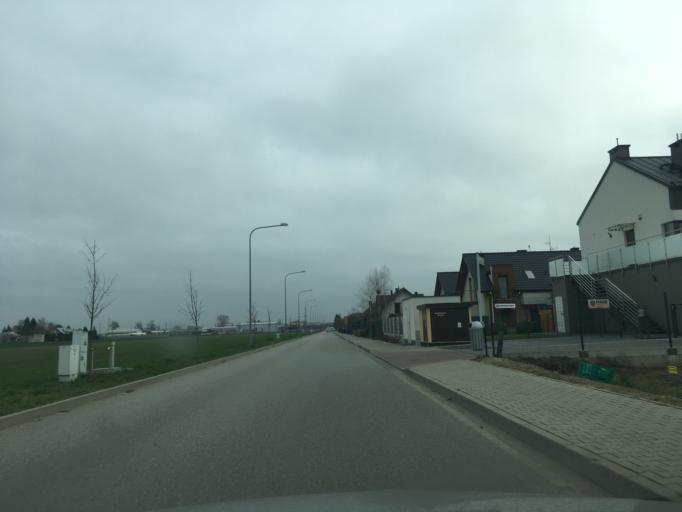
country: PL
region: Masovian Voivodeship
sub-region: Powiat piaseczynski
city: Lesznowola
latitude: 52.0832
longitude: 20.9514
